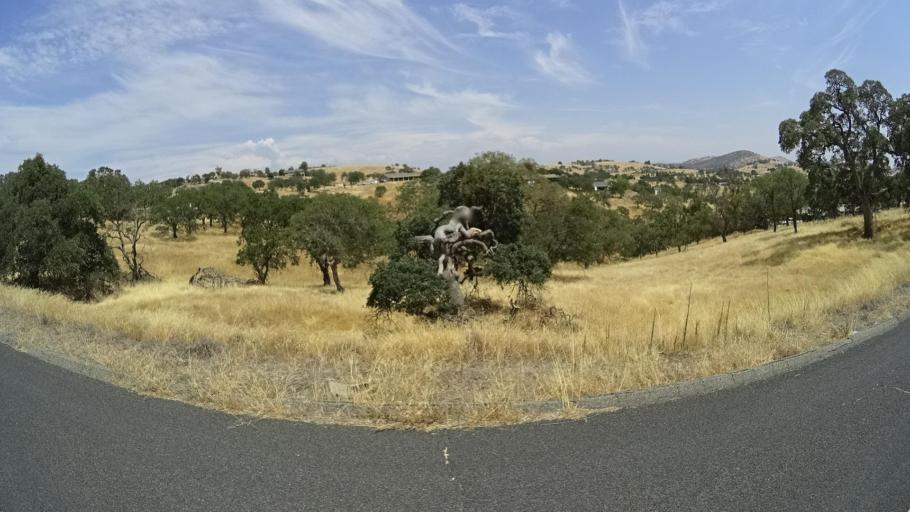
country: US
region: California
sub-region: Tuolumne County
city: Jamestown
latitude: 37.6491
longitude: -120.3540
